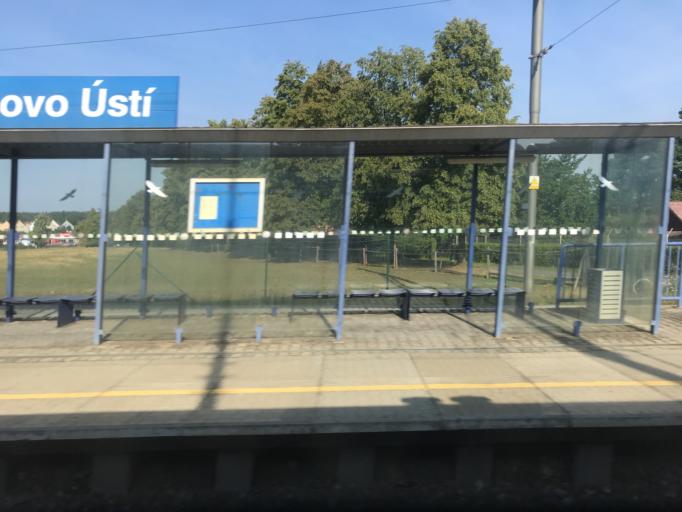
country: CZ
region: Jihocesky
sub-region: Okres Tabor
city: Sezimovo Usti
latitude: 49.3801
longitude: 14.6975
